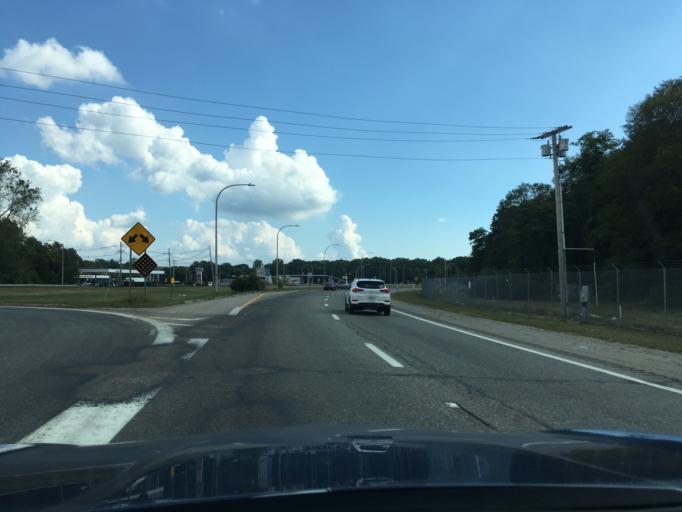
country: US
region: Massachusetts
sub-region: Bristol County
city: Seekonk
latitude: 41.7904
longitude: -71.3352
